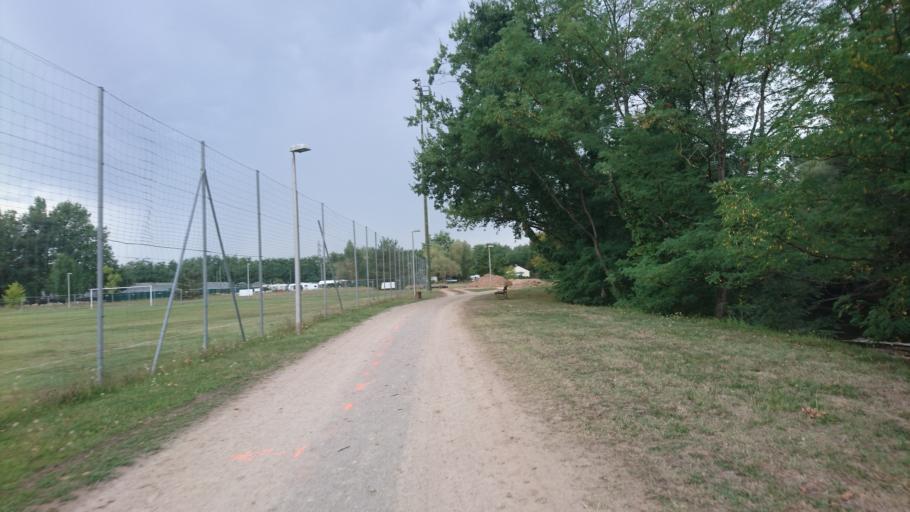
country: FR
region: Limousin
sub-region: Departement de la Correze
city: Ussac
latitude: 45.1581
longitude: 1.4878
